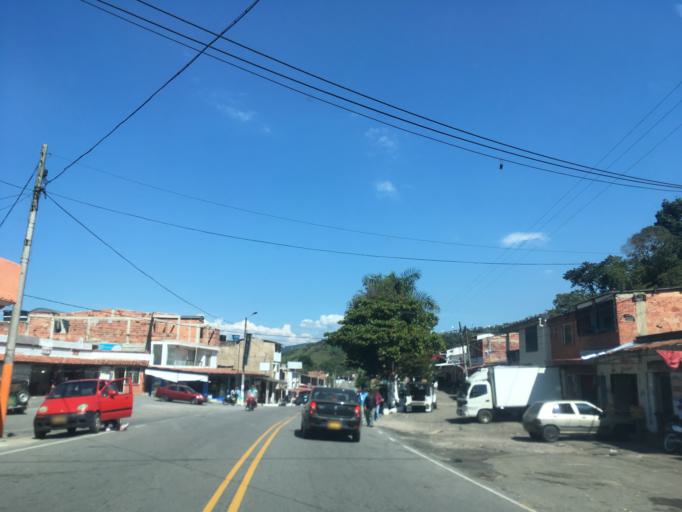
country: CO
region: Santander
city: Suaita
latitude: 6.0688
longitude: -73.4140
